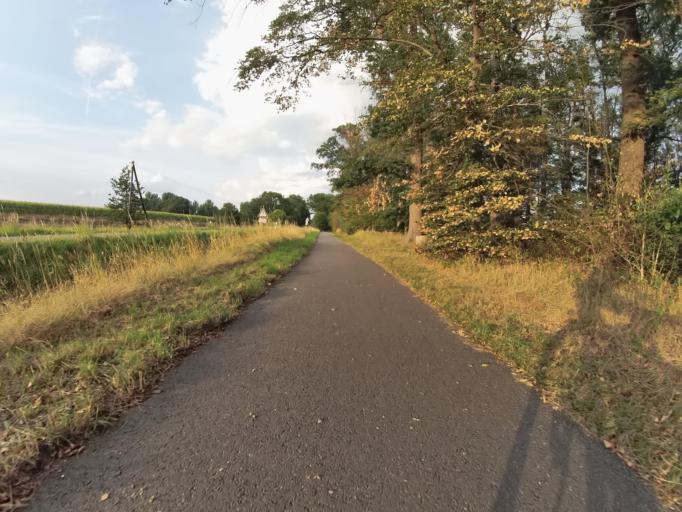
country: DE
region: North Rhine-Westphalia
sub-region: Regierungsbezirk Munster
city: Westerkappeln
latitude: 52.3597
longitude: 7.8920
